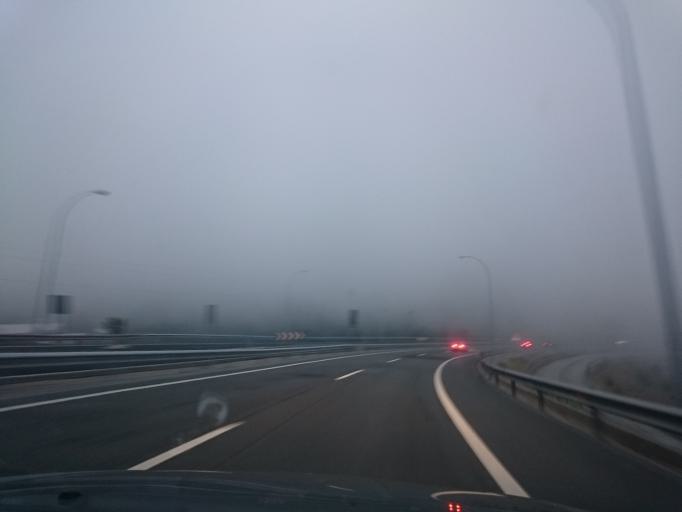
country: ES
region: Castille and Leon
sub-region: Provincia de Leon
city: Sena de Luna
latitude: 42.9810
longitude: -5.8311
